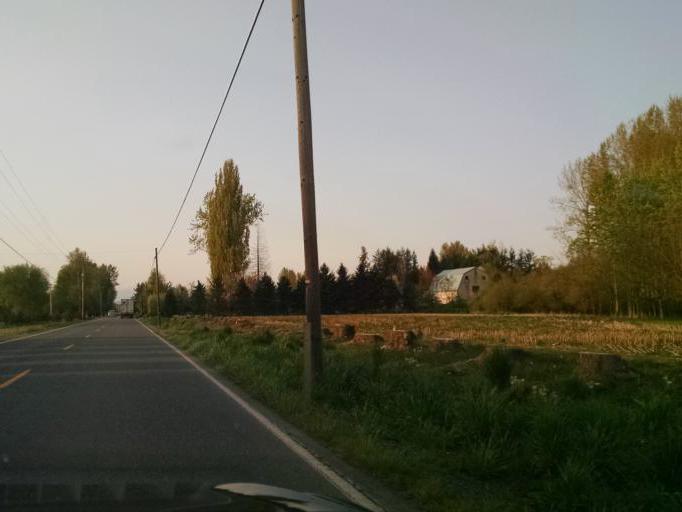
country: US
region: Washington
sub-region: Whatcom County
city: Nooksack
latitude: 48.8926
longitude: -122.3206
